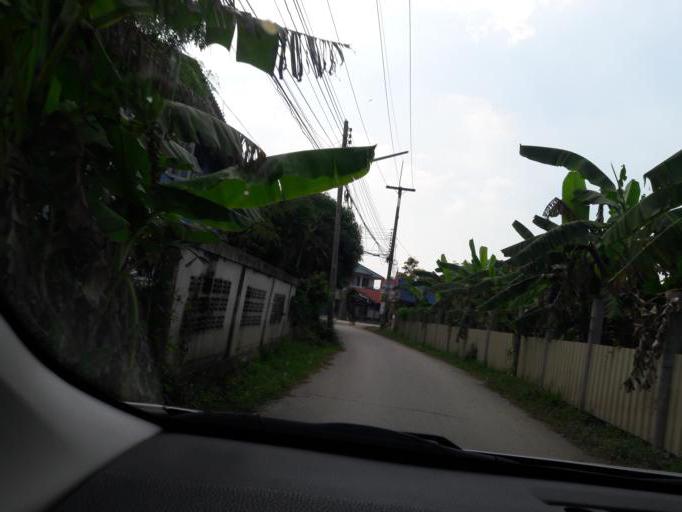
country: TH
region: Ang Thong
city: Ang Thong
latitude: 14.5708
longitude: 100.4143
